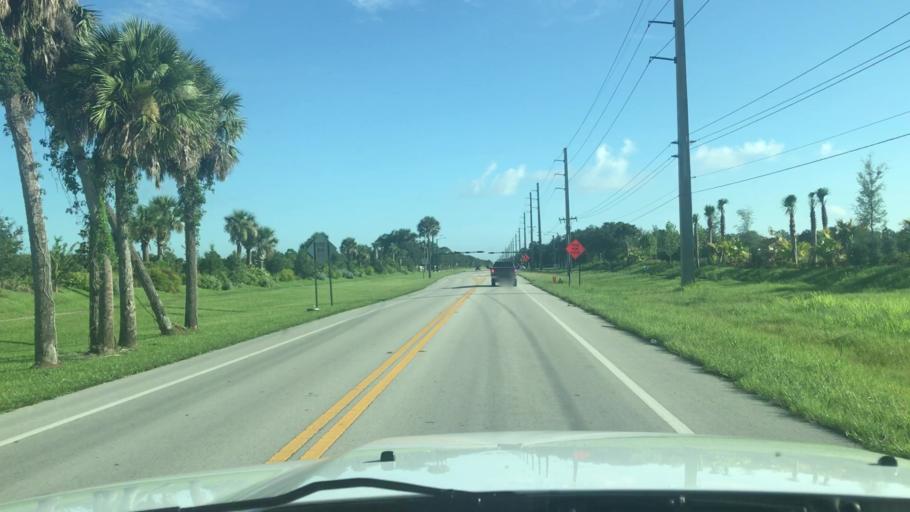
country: US
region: Florida
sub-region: Saint Lucie County
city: Lakewood Park
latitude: 27.5626
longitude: -80.4145
